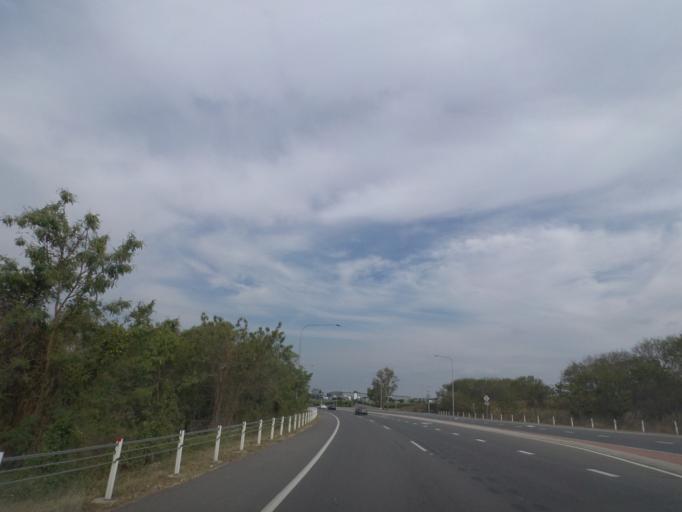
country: AU
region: Queensland
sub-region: Brisbane
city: Inala
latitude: -27.5976
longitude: 153.0106
